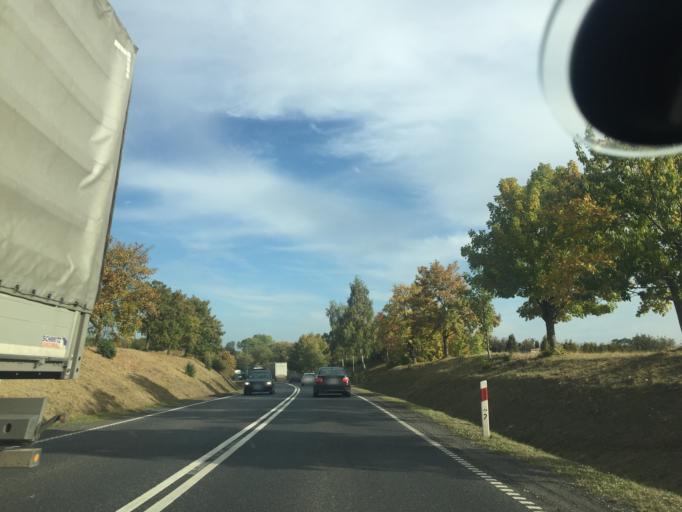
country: PL
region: Greater Poland Voivodeship
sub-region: Powiat gnieznienski
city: Trzemeszno
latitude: 52.5672
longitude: 17.8334
